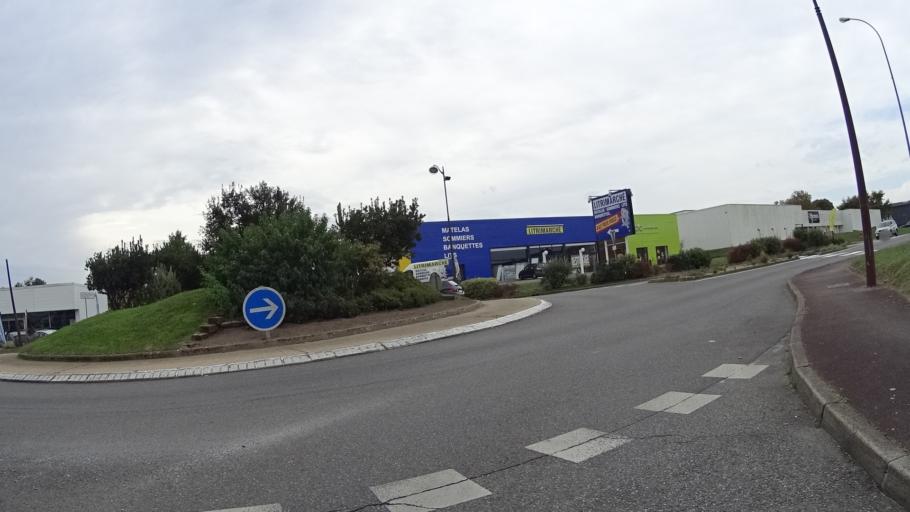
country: FR
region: Aquitaine
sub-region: Departement des Landes
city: Saint-Paul-les-Dax
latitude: 43.7268
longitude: -1.0782
